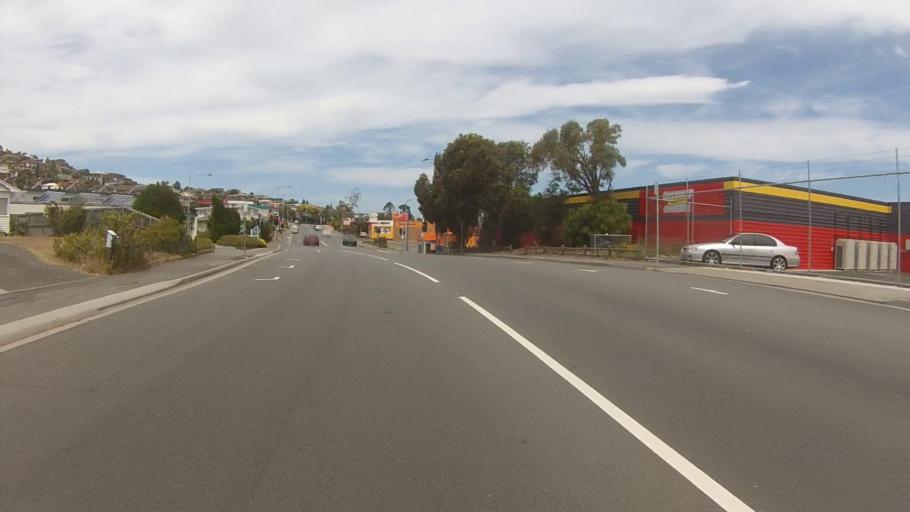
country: AU
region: Tasmania
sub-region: Clarence
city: Bellerive
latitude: -42.8643
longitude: 147.3718
